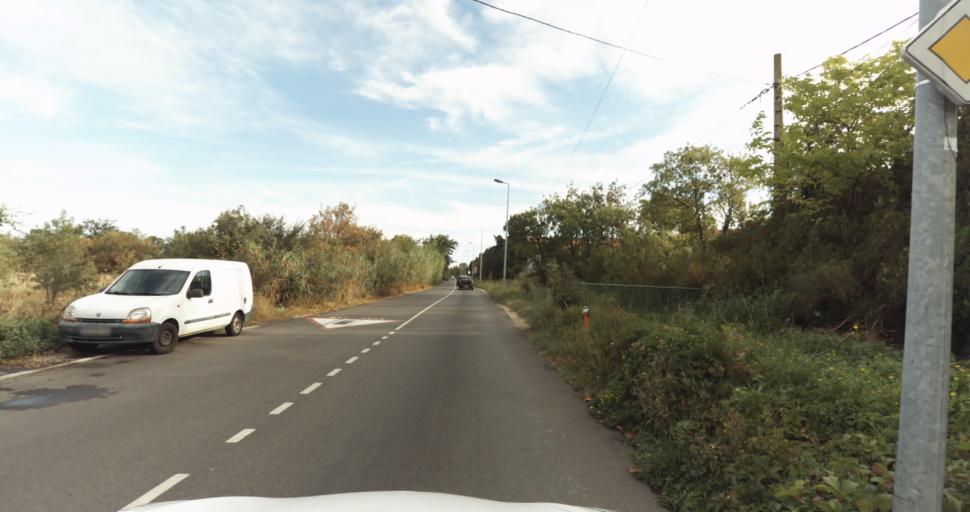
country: FR
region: Provence-Alpes-Cote d'Azur
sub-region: Departement des Bouches-du-Rhone
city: Miramas
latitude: 43.5834
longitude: 4.9949
